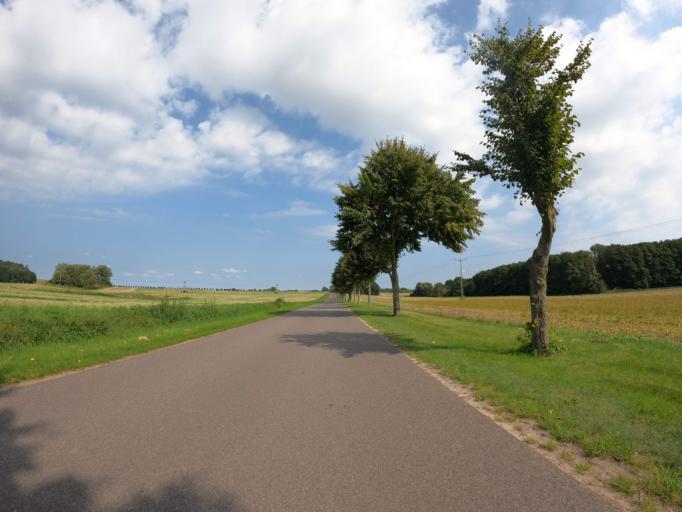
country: DE
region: Mecklenburg-Vorpommern
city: Malchow
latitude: 53.4528
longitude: 12.4698
